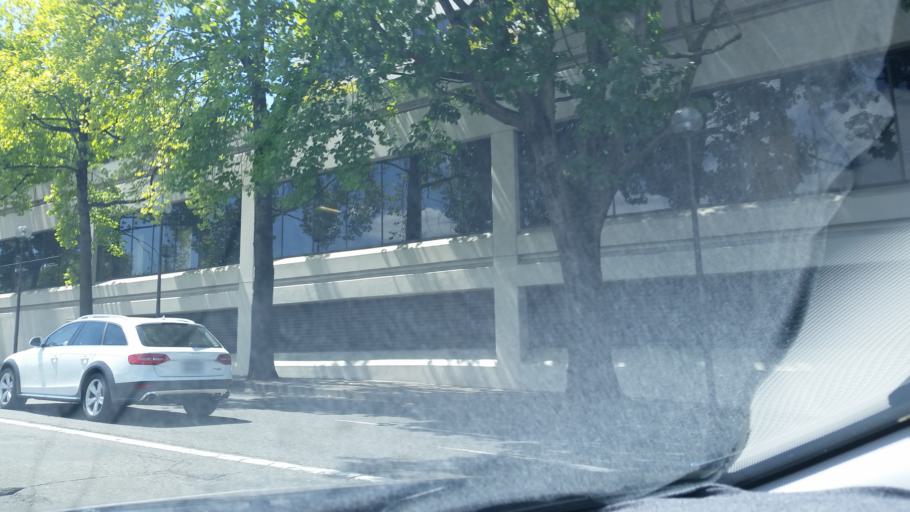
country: US
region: Oregon
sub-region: Multnomah County
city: Portland
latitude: 45.5120
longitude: -122.6756
